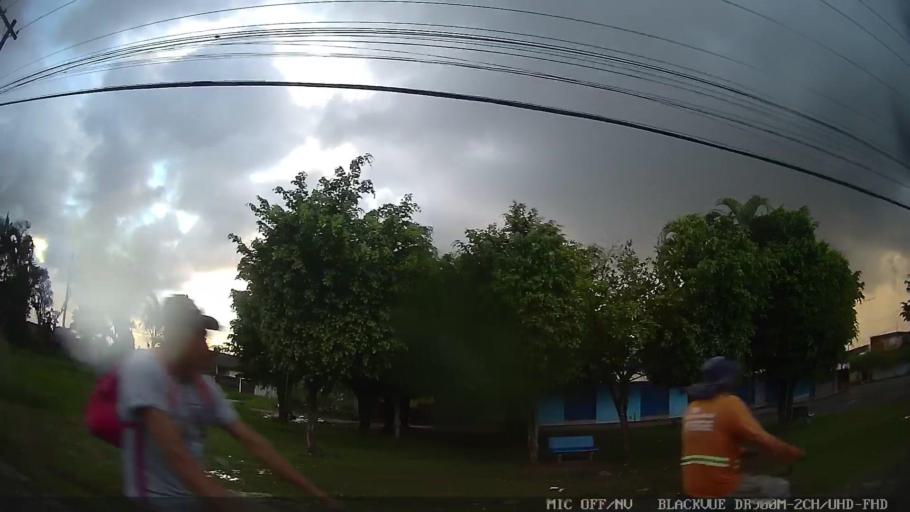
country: BR
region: Sao Paulo
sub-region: Itanhaem
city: Itanhaem
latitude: -24.1552
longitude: -46.7804
